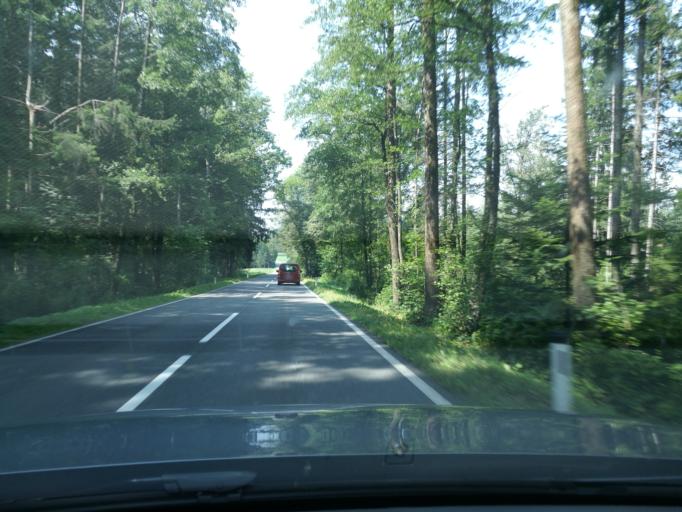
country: AT
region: Upper Austria
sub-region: Politischer Bezirk Grieskirchen
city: Grieskirchen
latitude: 48.3514
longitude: 13.7205
